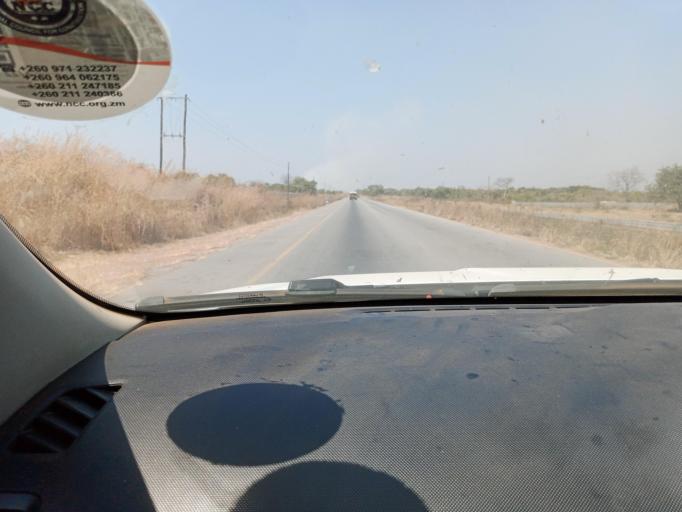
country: ZM
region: Copperbelt
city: Kitwe
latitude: -12.9122
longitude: 28.3414
